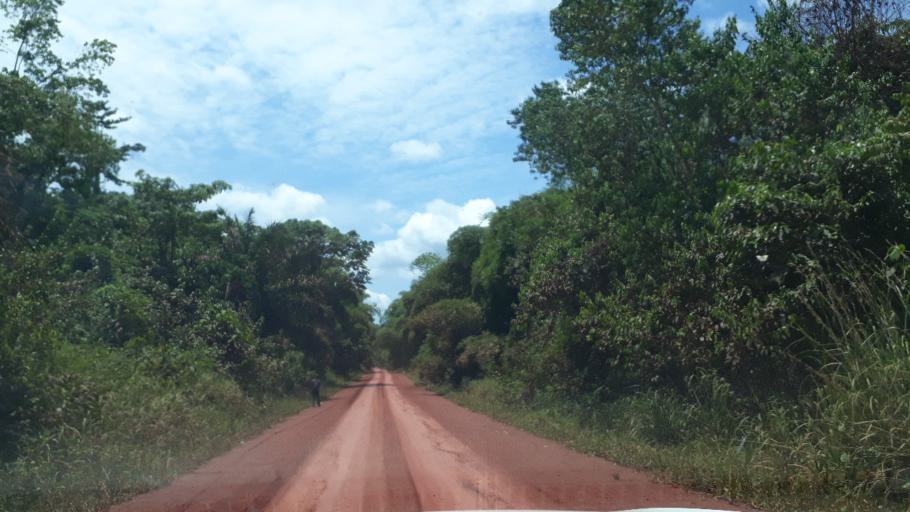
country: CD
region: Eastern Province
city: Kisangani
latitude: 0.5417
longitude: 25.8267
